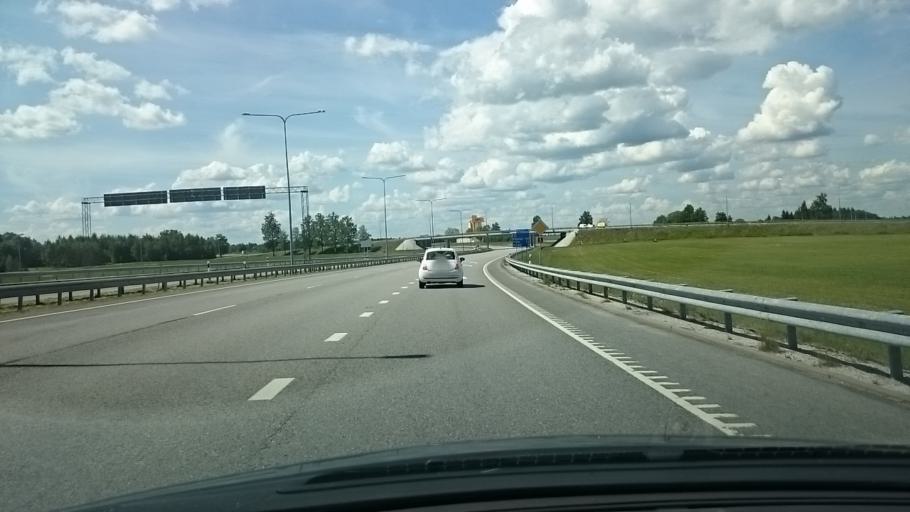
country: EE
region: Jaervamaa
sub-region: Paide linn
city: Paide
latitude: 58.9175
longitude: 25.6166
